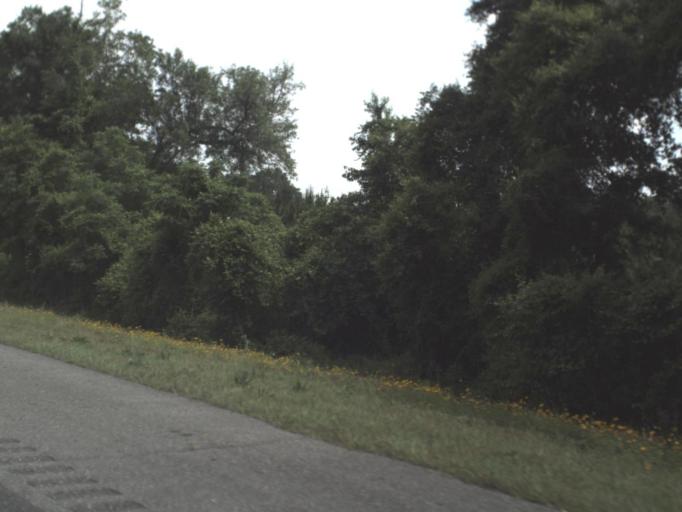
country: US
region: Florida
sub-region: Suwannee County
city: Live Oak
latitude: 30.3114
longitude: -82.9327
